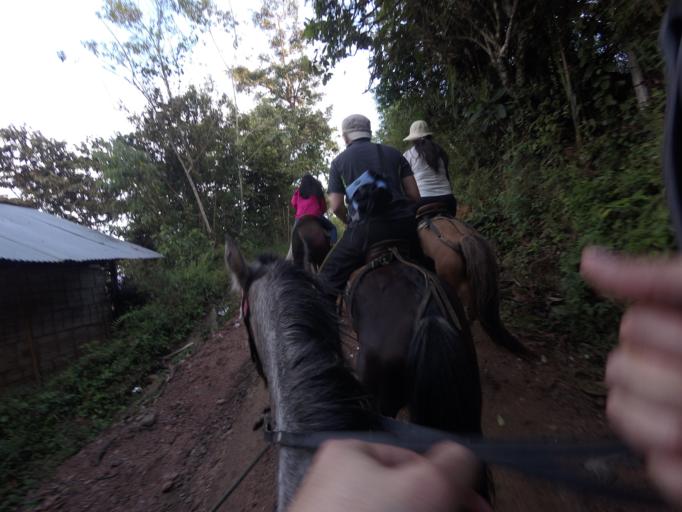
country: CO
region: Huila
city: San Agustin
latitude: 1.8983
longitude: -76.2758
